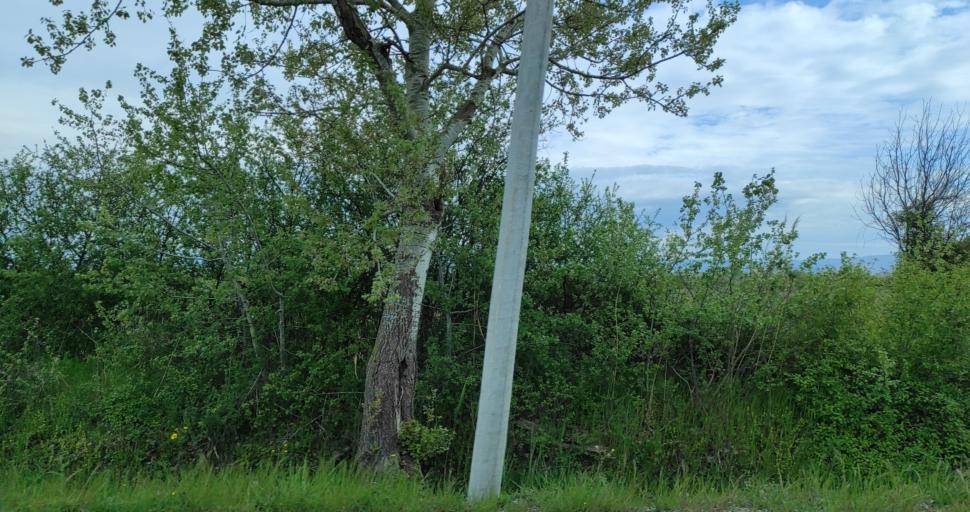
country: AL
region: Shkoder
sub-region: Rrethi i Shkodres
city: Dajc
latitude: 42.0138
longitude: 19.4256
